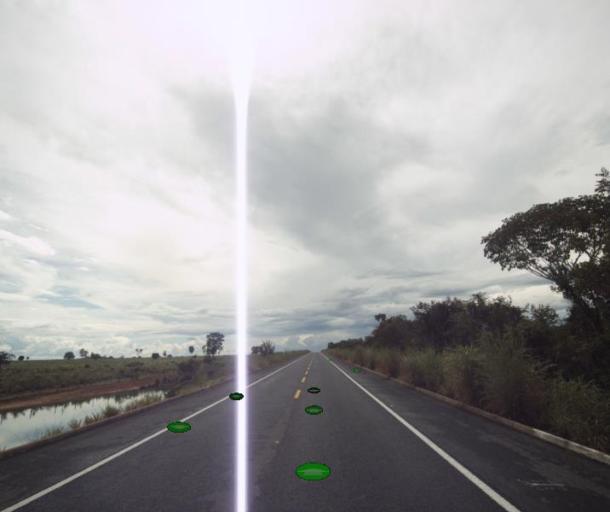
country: BR
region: Goias
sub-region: Sao Miguel Do Araguaia
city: Sao Miguel do Araguaia
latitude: -13.2732
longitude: -50.5036
